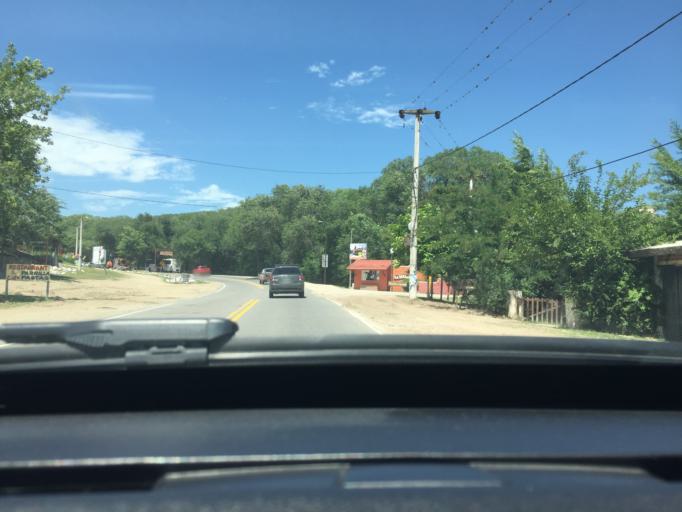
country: AR
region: Cordoba
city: Alta Gracia
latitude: -31.7365
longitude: -64.4516
